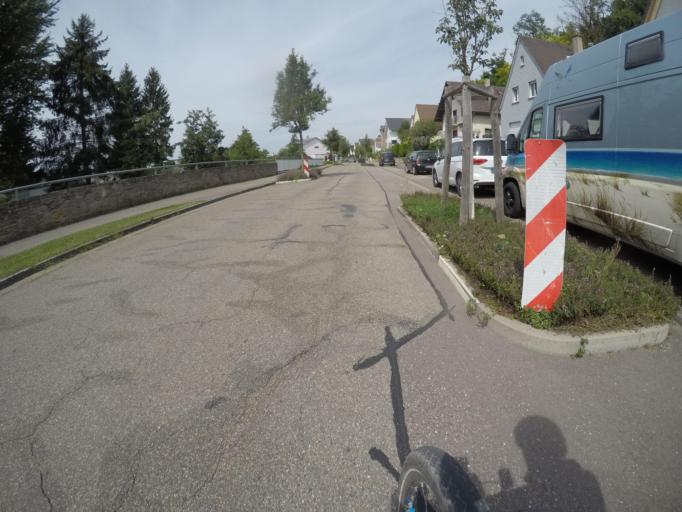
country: DE
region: Baden-Wuerttemberg
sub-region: Karlsruhe Region
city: Bruchsal
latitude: 49.1187
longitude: 8.6160
